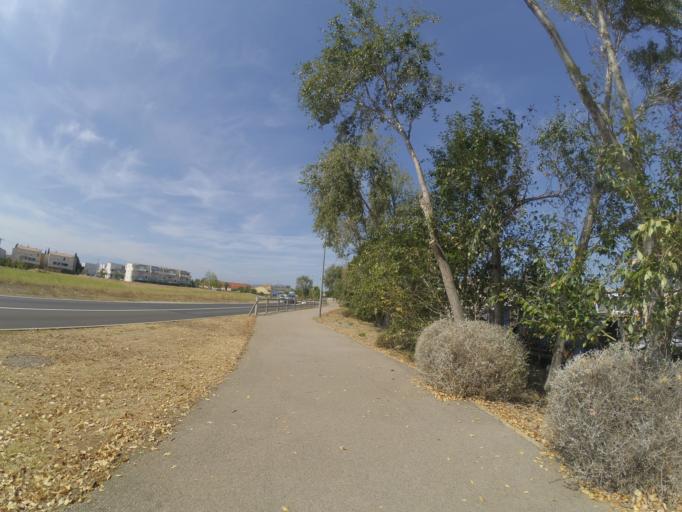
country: FR
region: Languedoc-Roussillon
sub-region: Departement des Pyrenees-Orientales
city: Rivesaltes
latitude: 42.7799
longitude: 2.8776
